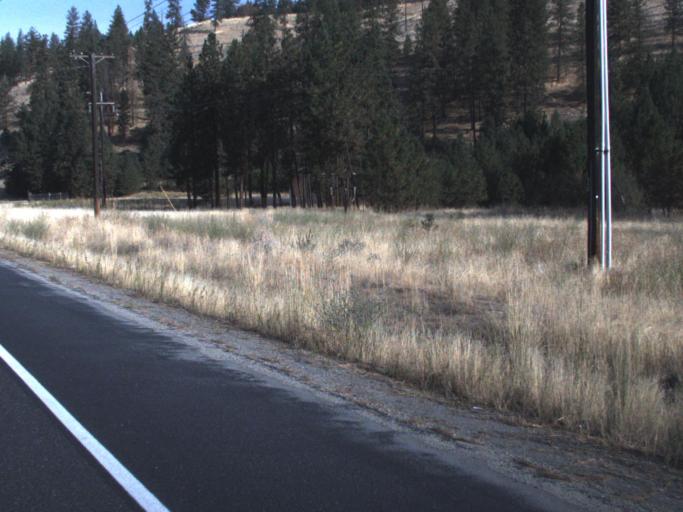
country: US
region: Washington
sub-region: Spokane County
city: Town and Country
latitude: 47.7565
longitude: -117.5179
